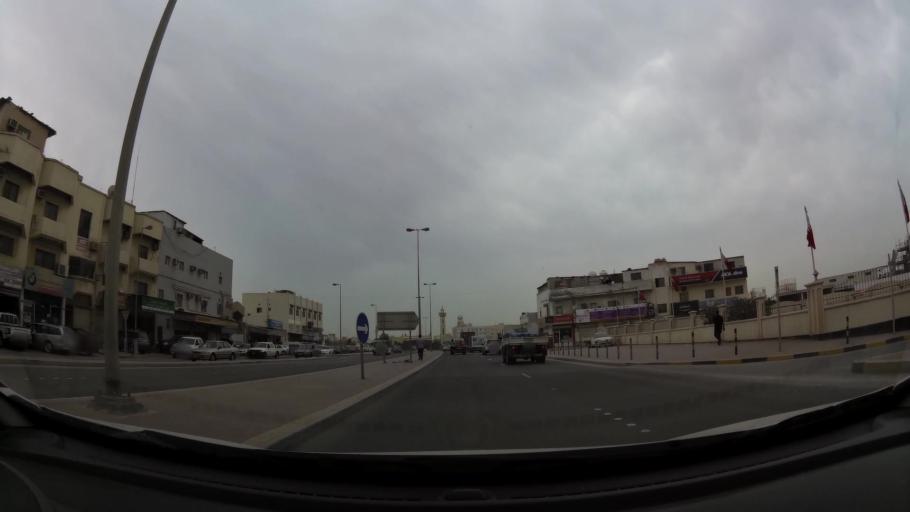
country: BH
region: Northern
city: Madinat `Isa
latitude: 26.1861
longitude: 50.5281
